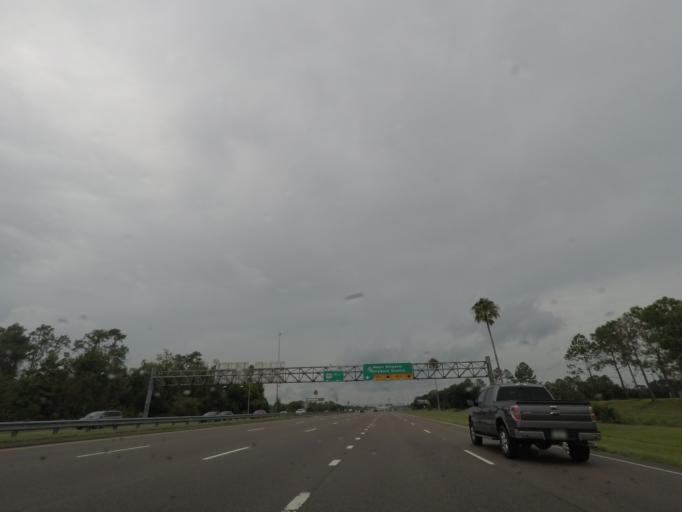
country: US
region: Florida
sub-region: Osceola County
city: Celebration
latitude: 28.3329
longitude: -81.5559
